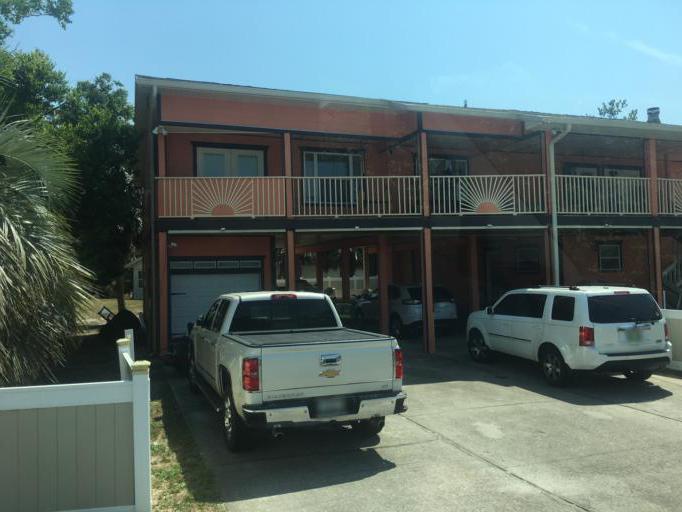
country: US
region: Florida
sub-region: Bay County
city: Lower Grand Lagoon
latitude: 30.1467
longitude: -85.7506
